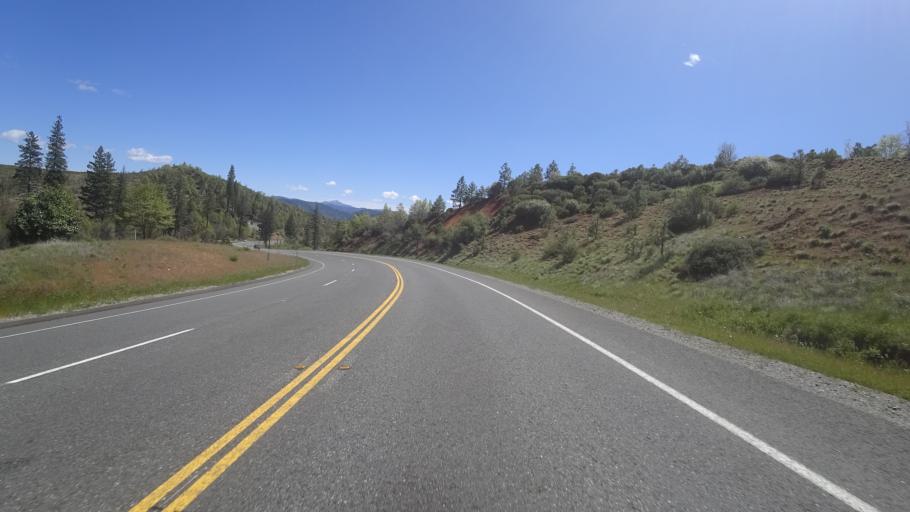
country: US
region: California
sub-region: Trinity County
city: Weaverville
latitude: 40.7445
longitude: -122.9712
